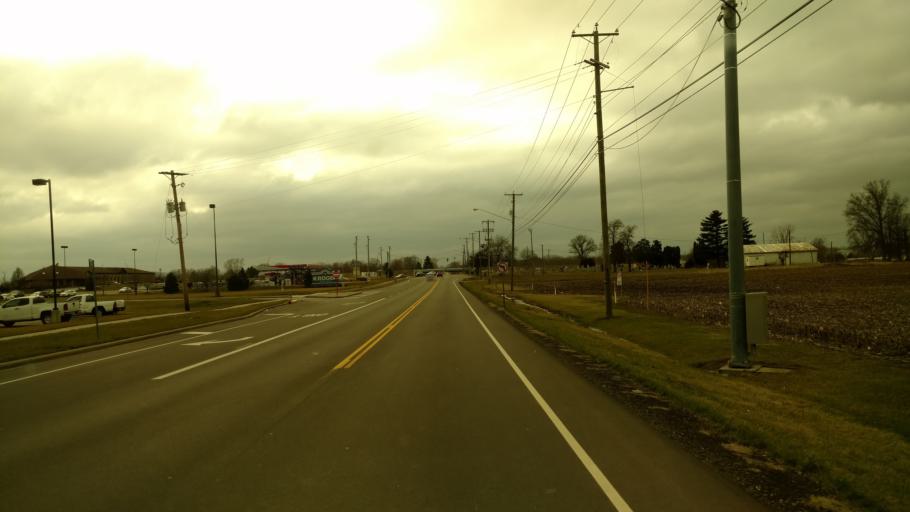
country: US
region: Ohio
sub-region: Licking County
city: Hebron
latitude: 39.9614
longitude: -82.4742
